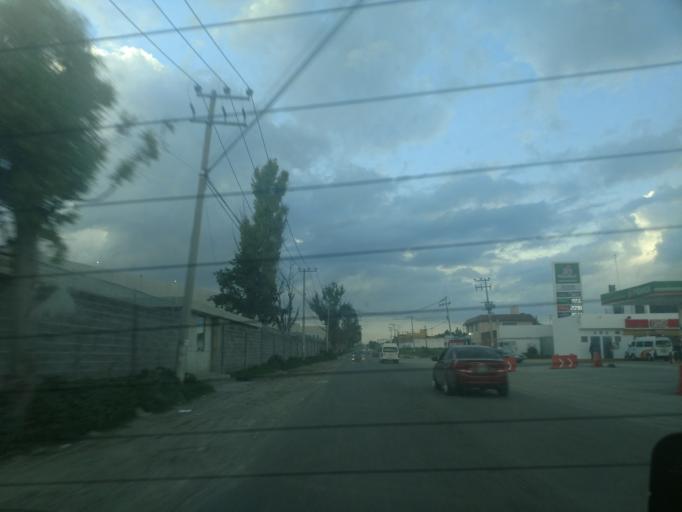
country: MX
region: Mexico
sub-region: Cuautitlan
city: Barrio Tlatenco
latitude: 19.7427
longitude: -99.1995
